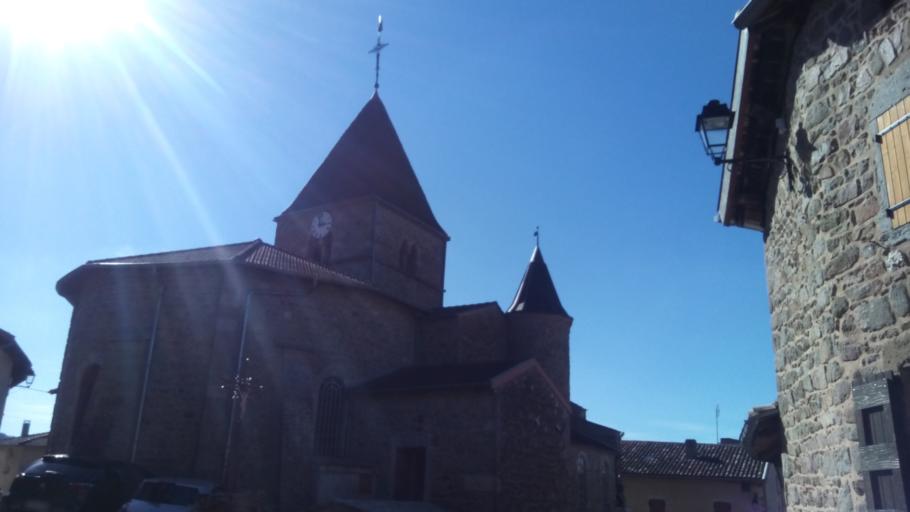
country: FR
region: Rhone-Alpes
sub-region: Departement du Rhone
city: Beaujeu
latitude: 46.2564
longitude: 4.5974
